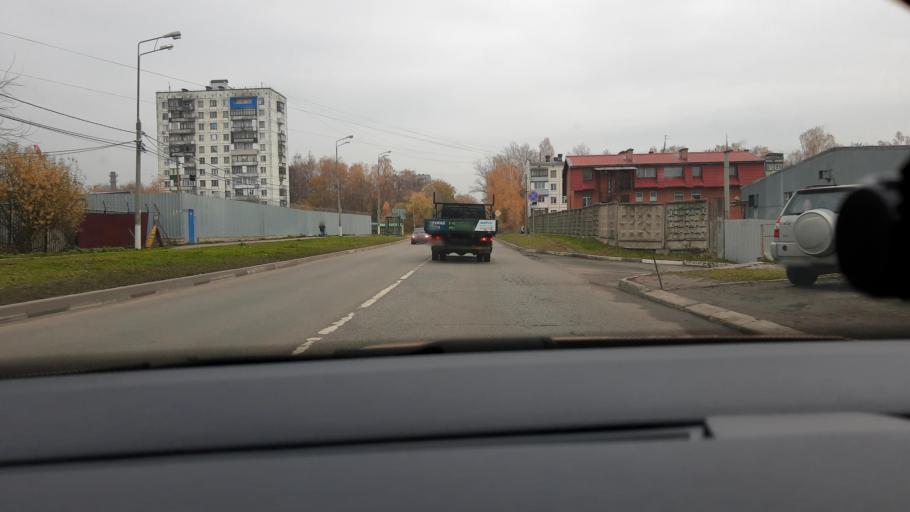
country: RU
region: Moskovskaya
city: Cherkizovo
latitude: 55.9399
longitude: 37.7710
